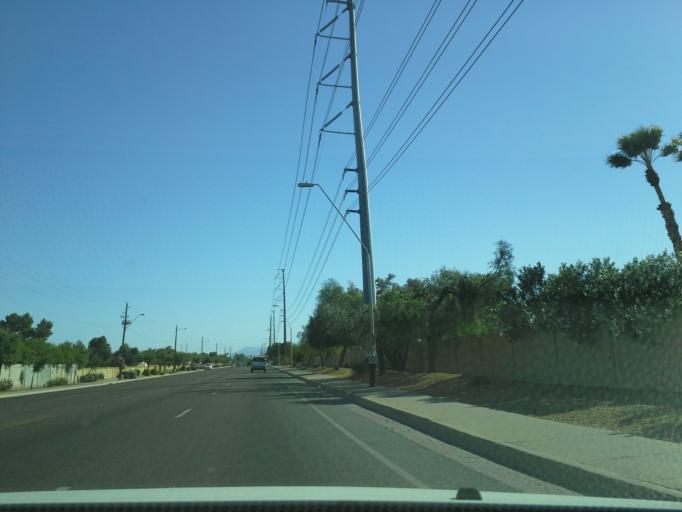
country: US
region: Arizona
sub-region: Maricopa County
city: Peoria
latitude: 33.5727
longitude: -112.2029
